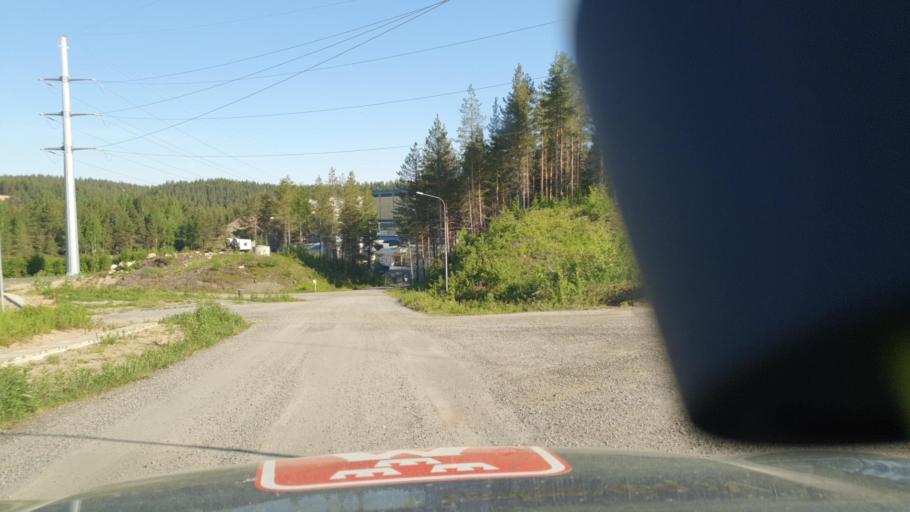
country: SE
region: Norrbotten
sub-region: Alvsbyns Kommun
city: AElvsbyn
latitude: 66.2221
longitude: 20.8631
